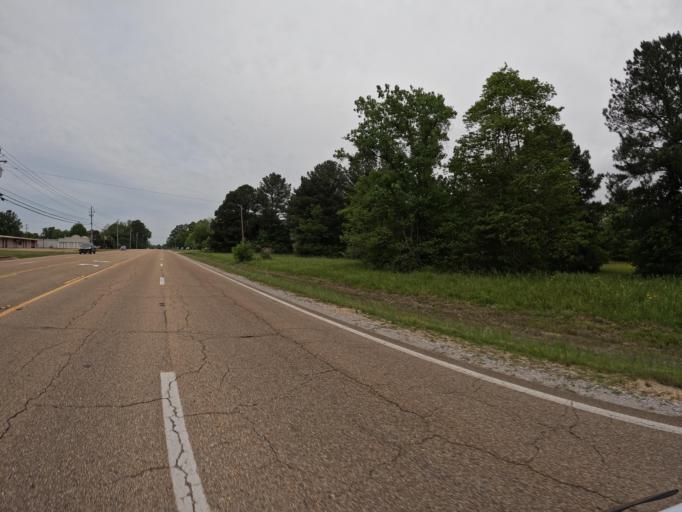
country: US
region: Mississippi
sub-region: Lee County
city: Tupelo
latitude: 34.2932
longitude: -88.7577
